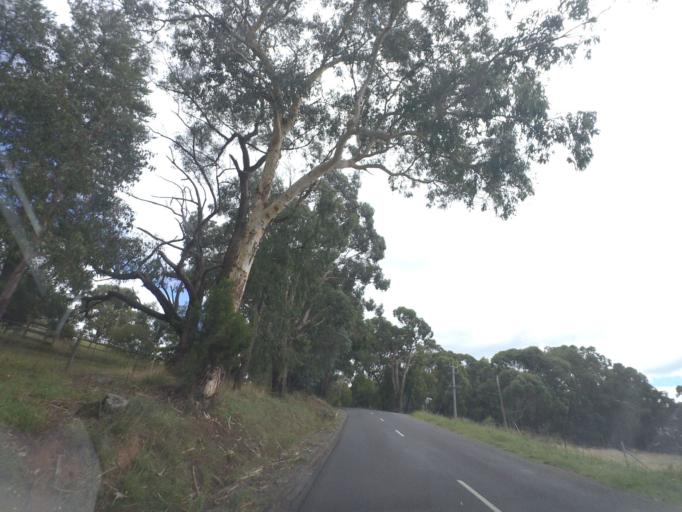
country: AU
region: Victoria
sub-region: Yarra Ranges
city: Woori Yallock
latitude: -37.8017
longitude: 145.4773
